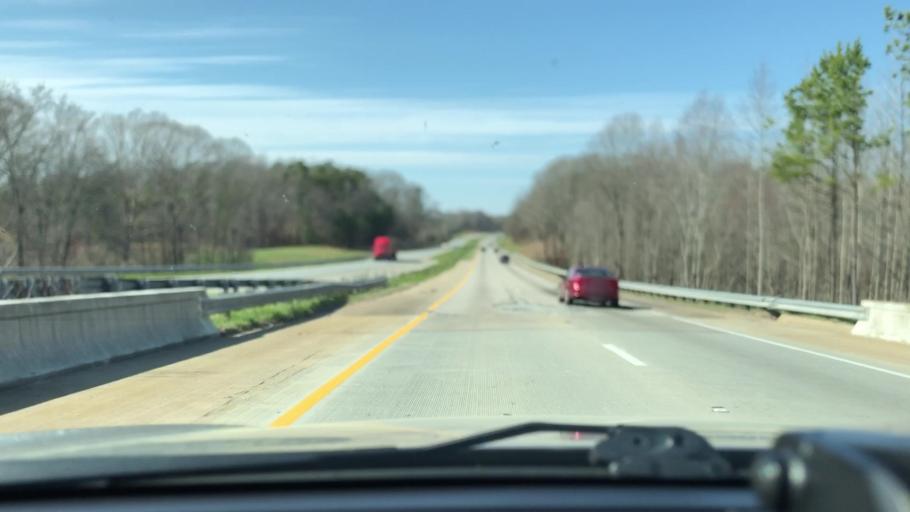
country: US
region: South Carolina
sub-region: Spartanburg County
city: Roebuck
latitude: 34.8608
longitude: -81.9818
